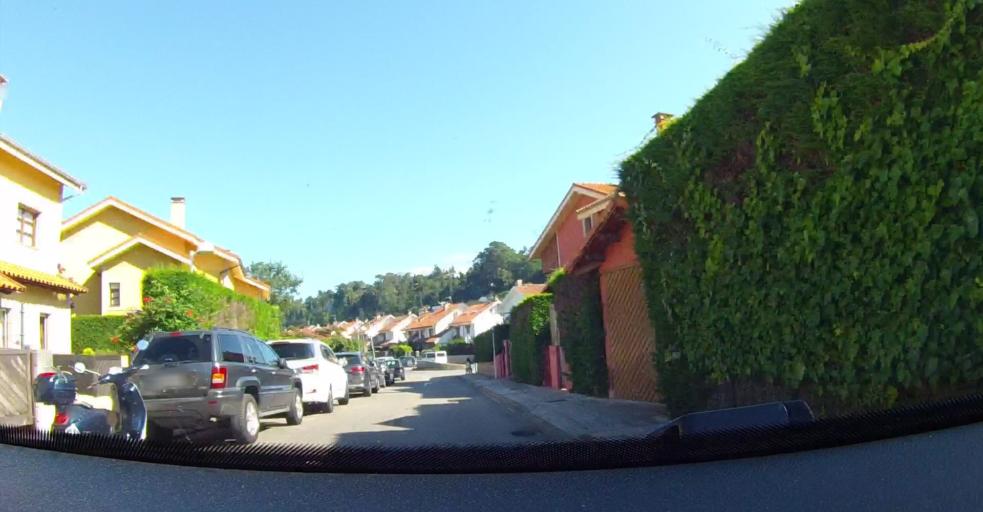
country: ES
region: Asturias
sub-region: Province of Asturias
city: Ribadesella
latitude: 43.4672
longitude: -5.0779
